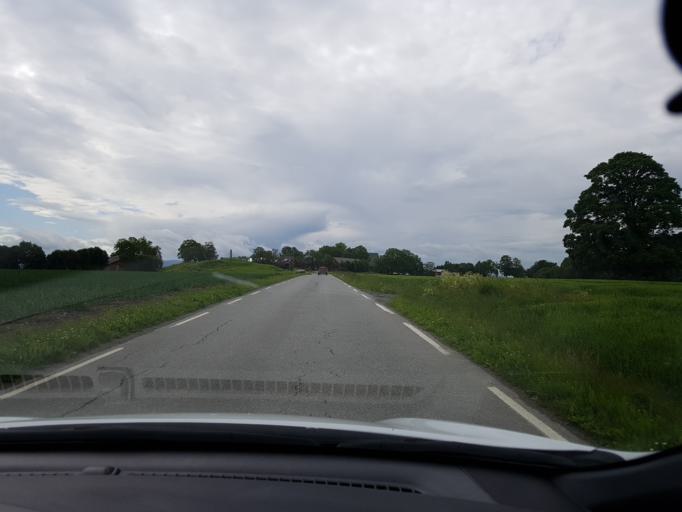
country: NO
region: Nord-Trondelag
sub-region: Frosta
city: Frosta
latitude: 63.5705
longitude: 10.7047
